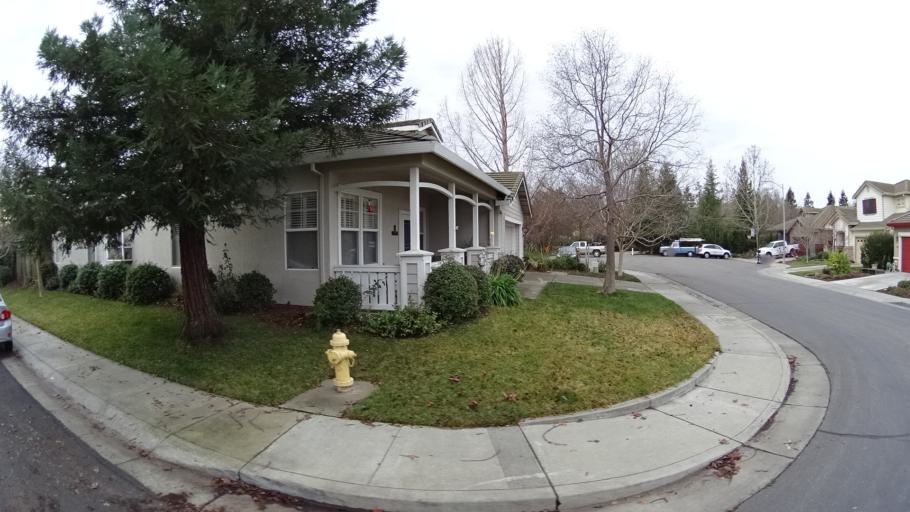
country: US
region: California
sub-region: Yolo County
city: Davis
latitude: 38.5668
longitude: -121.7258
